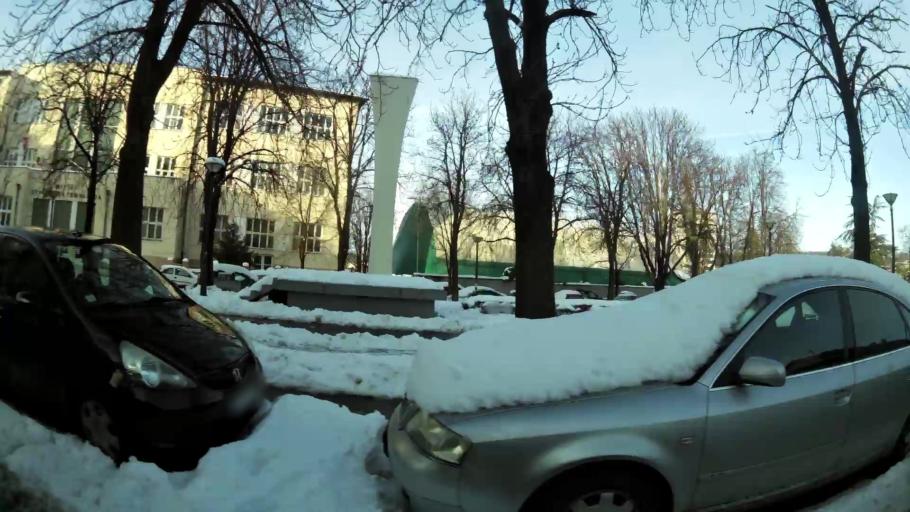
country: RS
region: Central Serbia
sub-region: Belgrade
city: Vracar
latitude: 44.7980
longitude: 20.4973
